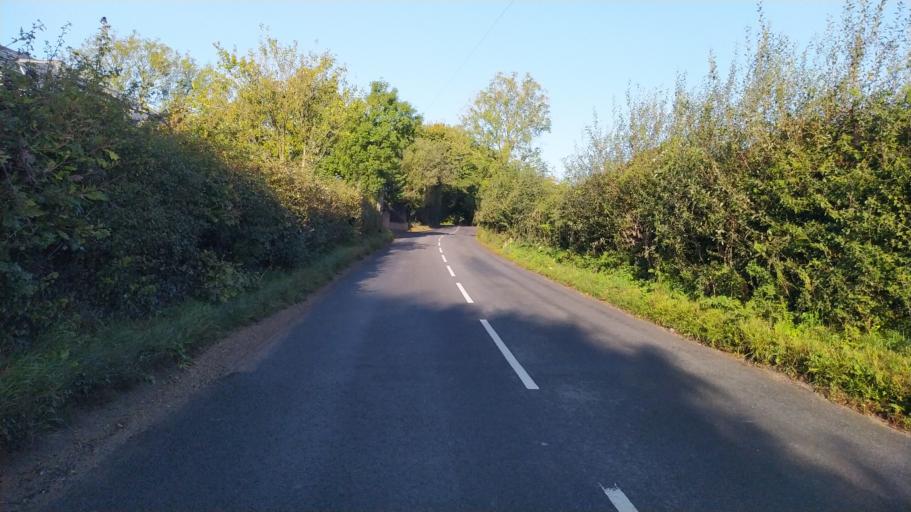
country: GB
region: England
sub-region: Dorset
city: Three Legged Cross
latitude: 50.8621
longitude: -1.9339
